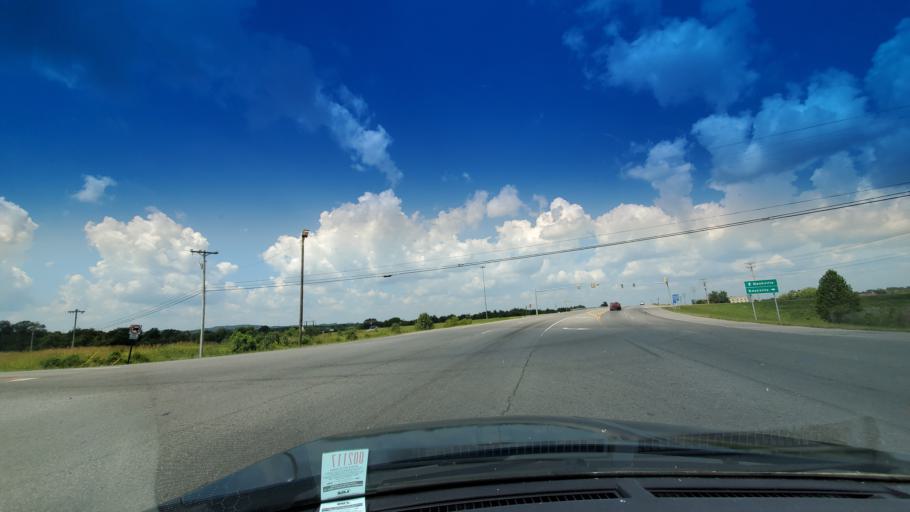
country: US
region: Tennessee
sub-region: Wilson County
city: Lebanon
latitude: 36.1801
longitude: -86.3260
